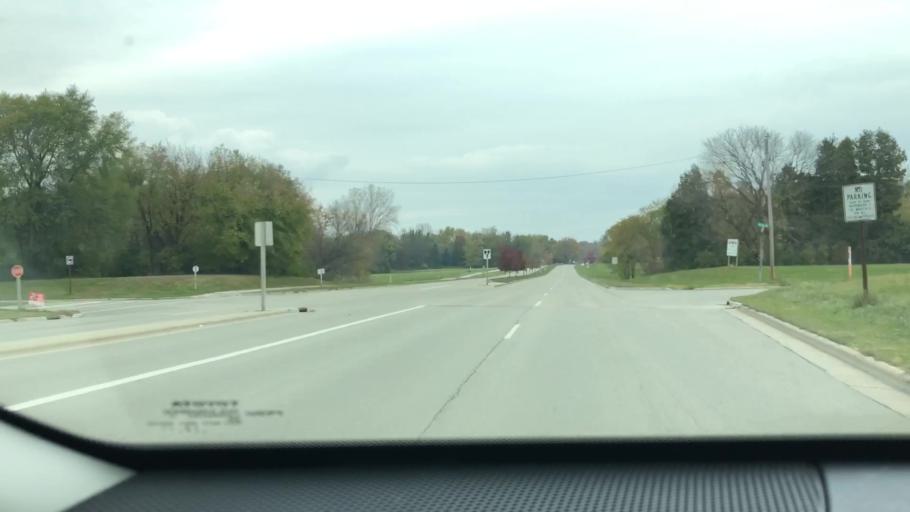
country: US
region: Wisconsin
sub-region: Brown County
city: Ashwaubenon
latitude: 44.4967
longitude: -88.1038
